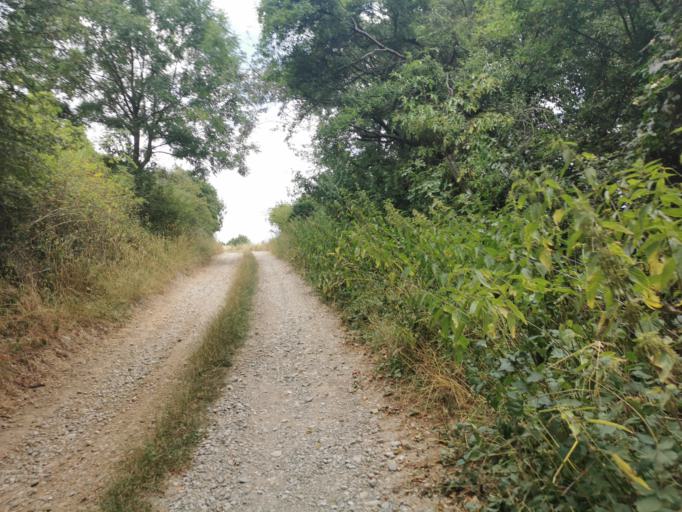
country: SK
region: Nitriansky
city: Brezova pod Bradlom
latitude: 48.6793
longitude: 17.5019
